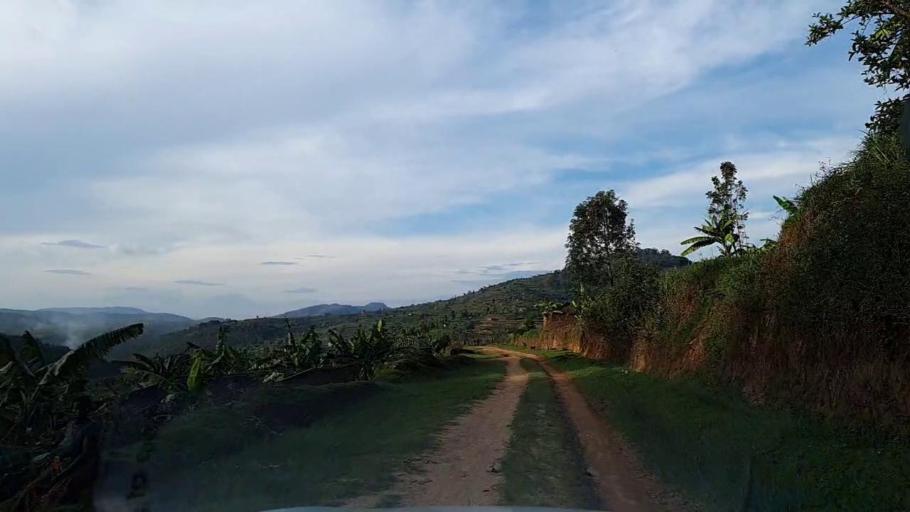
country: RW
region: Southern Province
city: Gikongoro
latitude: -2.4034
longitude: 29.5554
